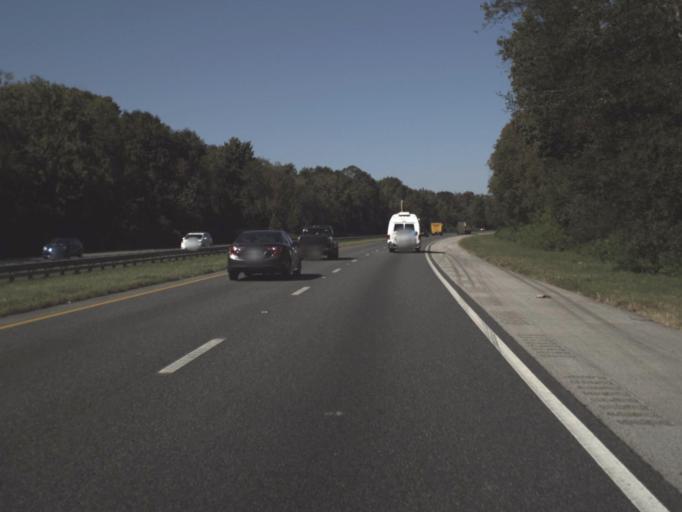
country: US
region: Florida
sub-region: Sumter County
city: Wildwood
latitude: 28.8486
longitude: -82.0806
